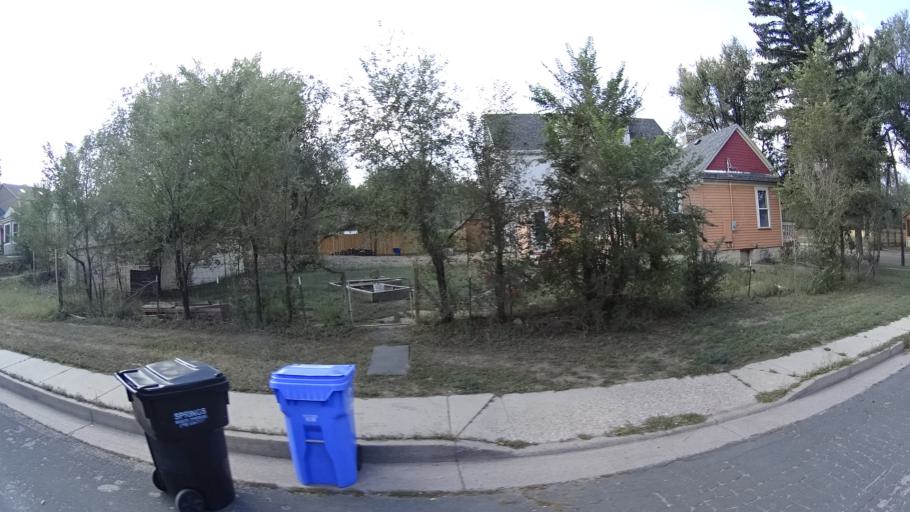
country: US
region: Colorado
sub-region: El Paso County
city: Colorado Springs
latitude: 38.8293
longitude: -104.8129
